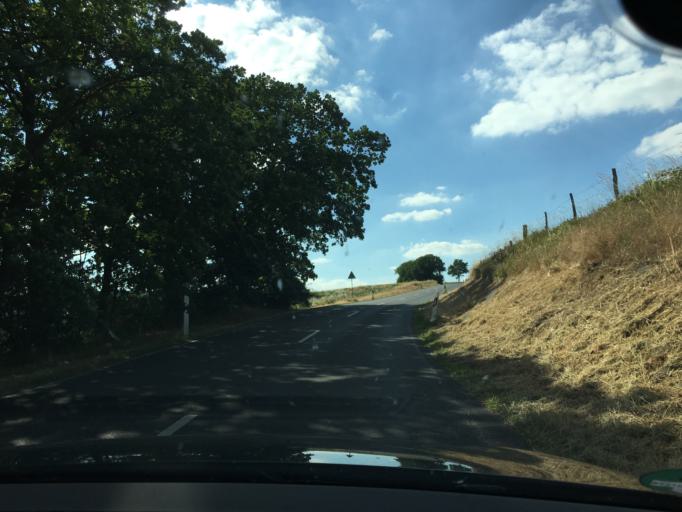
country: DE
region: North Rhine-Westphalia
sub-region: Regierungsbezirk Koln
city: Kreuzau
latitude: 50.7322
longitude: 6.4486
